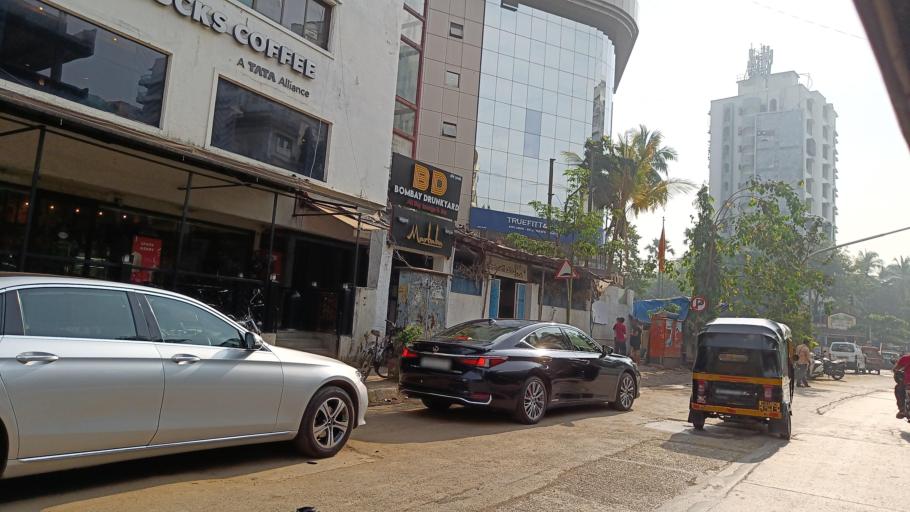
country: IN
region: Maharashtra
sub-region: Mumbai Suburban
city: Mumbai
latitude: 19.1147
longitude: 72.8362
